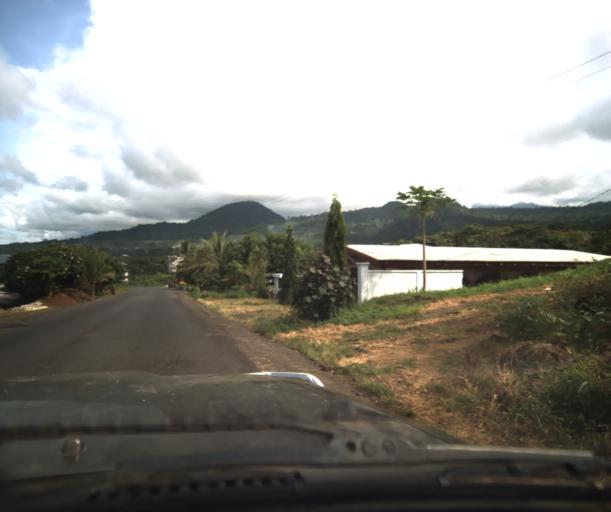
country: CM
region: South-West Province
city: Limbe
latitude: 4.0144
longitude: 9.1506
